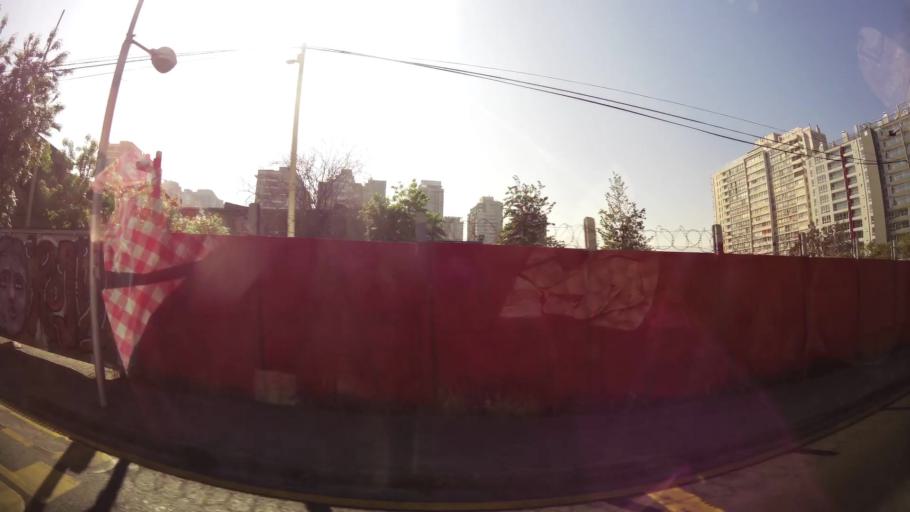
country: CL
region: Santiago Metropolitan
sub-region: Provincia de Santiago
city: Santiago
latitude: -33.4512
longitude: -70.6443
